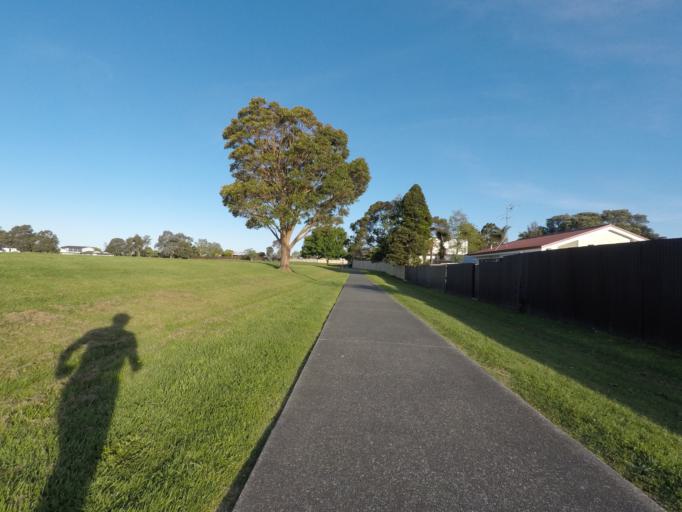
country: NZ
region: Auckland
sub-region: Auckland
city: Rosebank
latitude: -36.8394
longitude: 174.6425
